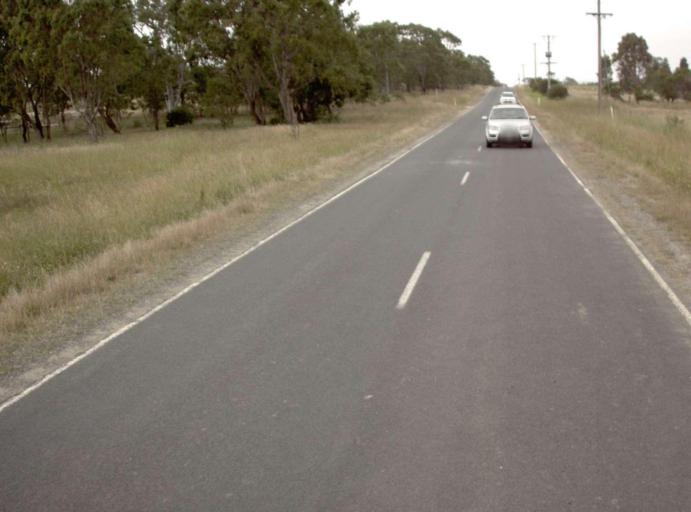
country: AU
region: Victoria
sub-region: Wellington
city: Heyfield
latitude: -38.0366
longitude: 146.7666
